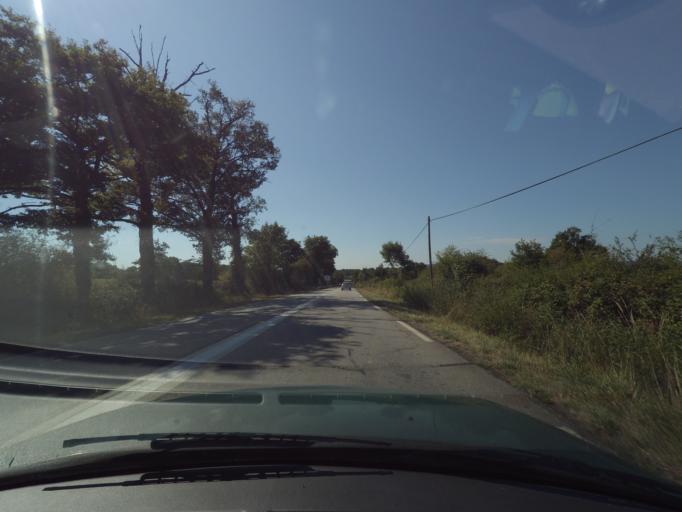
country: FR
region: Limousin
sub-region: Departement de la Haute-Vienne
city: Bellac
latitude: 46.1050
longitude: 1.0744
